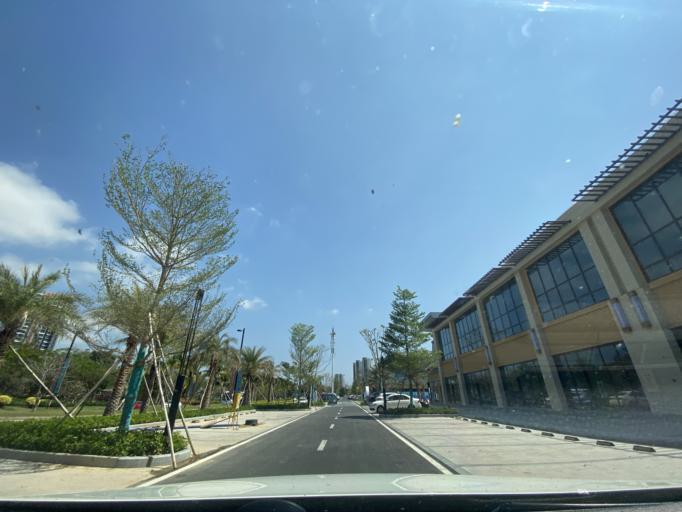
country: CN
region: Hainan
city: Xincun
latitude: 18.4196
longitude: 109.9107
